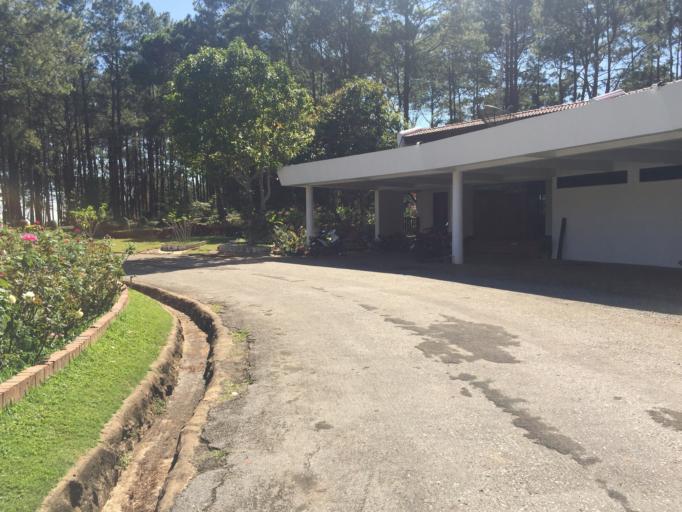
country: TH
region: Phetchabun
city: Khao Kho
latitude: 16.5530
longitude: 100.9755
